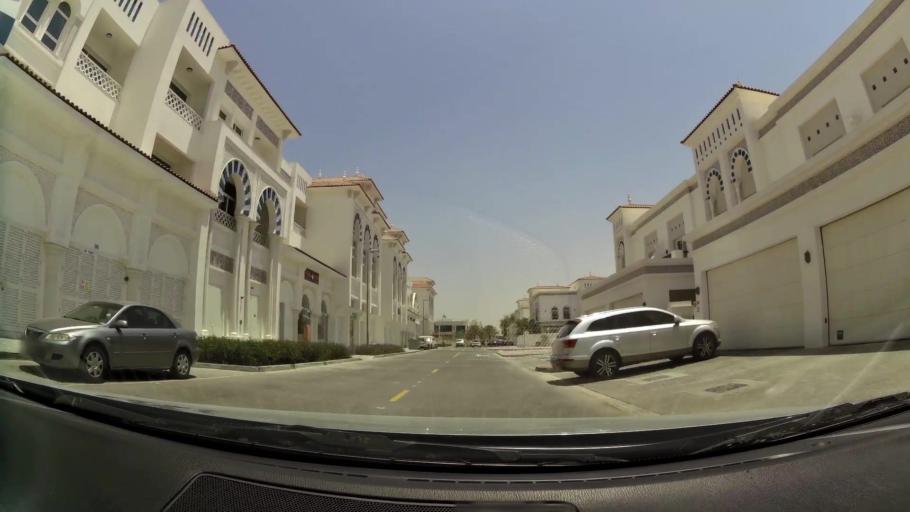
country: AE
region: Dubai
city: Dubai
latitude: 25.1948
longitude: 55.2463
